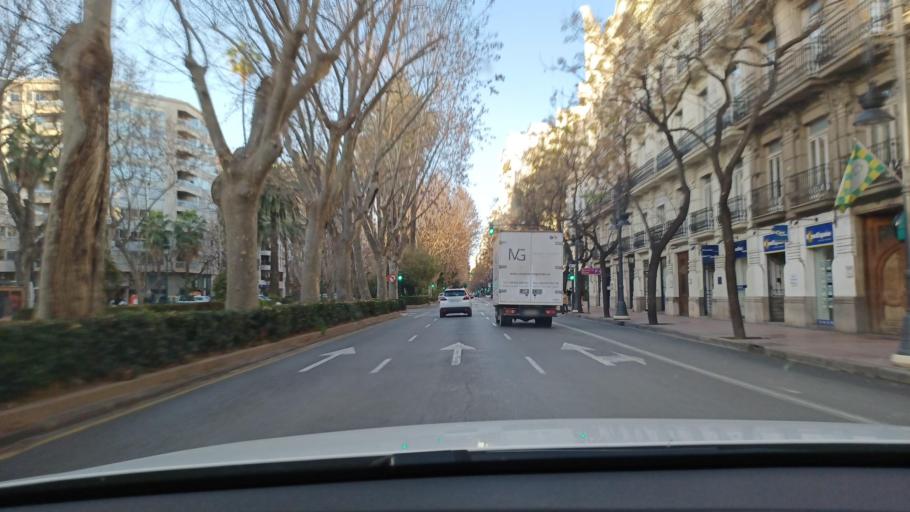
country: ES
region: Valencia
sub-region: Provincia de Valencia
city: Valencia
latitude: 39.4685
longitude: -0.3662
